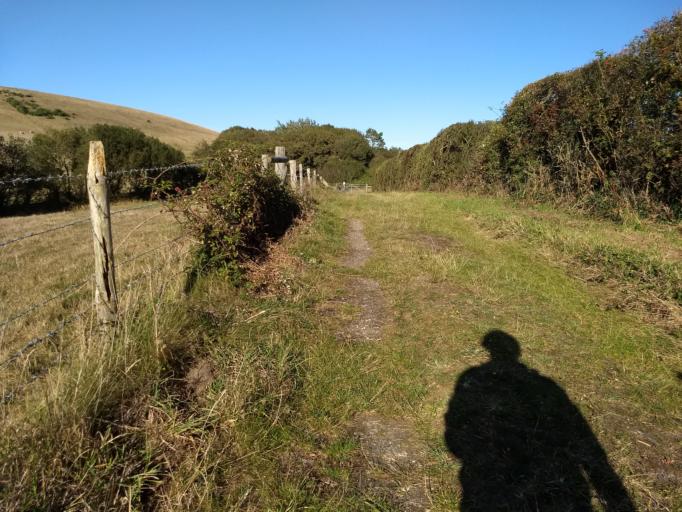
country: GB
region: England
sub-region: Isle of Wight
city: Newport
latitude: 50.6514
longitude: -1.2873
